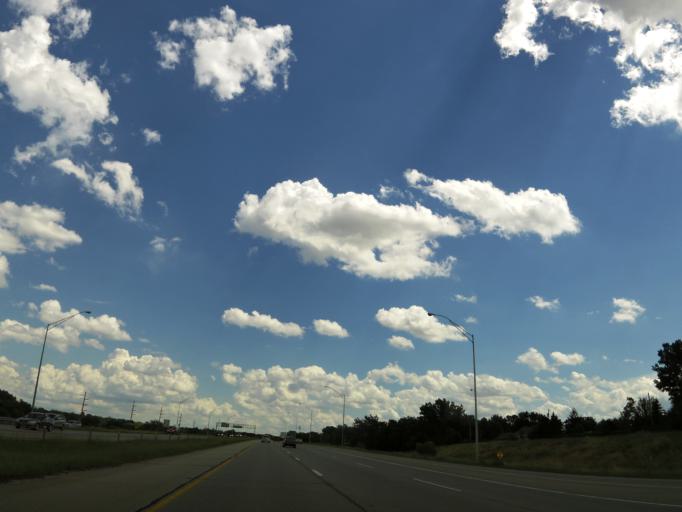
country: US
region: Iowa
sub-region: Linn County
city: Hiawatha
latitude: 42.0245
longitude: -91.6706
